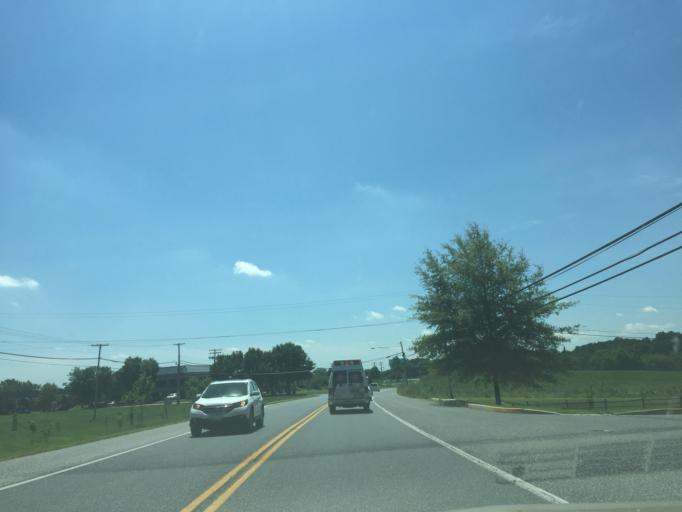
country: US
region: Maryland
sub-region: Harford County
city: Bel Air North
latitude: 39.5796
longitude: -76.3868
